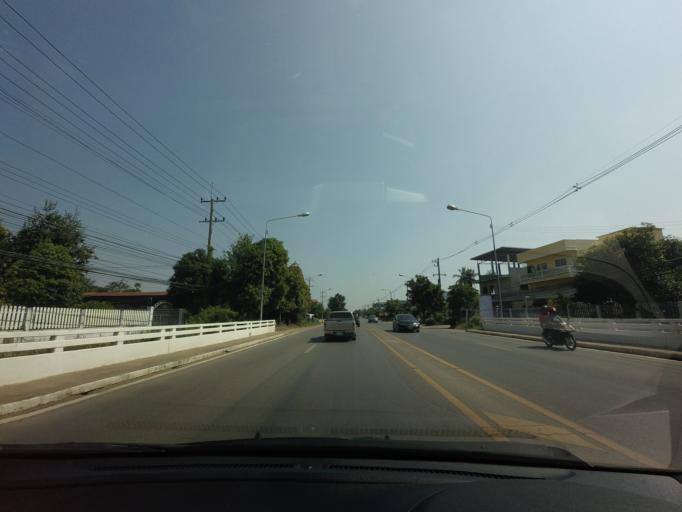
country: TH
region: Sukhothai
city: Sukhothai
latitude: 17.0109
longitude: 99.7845
